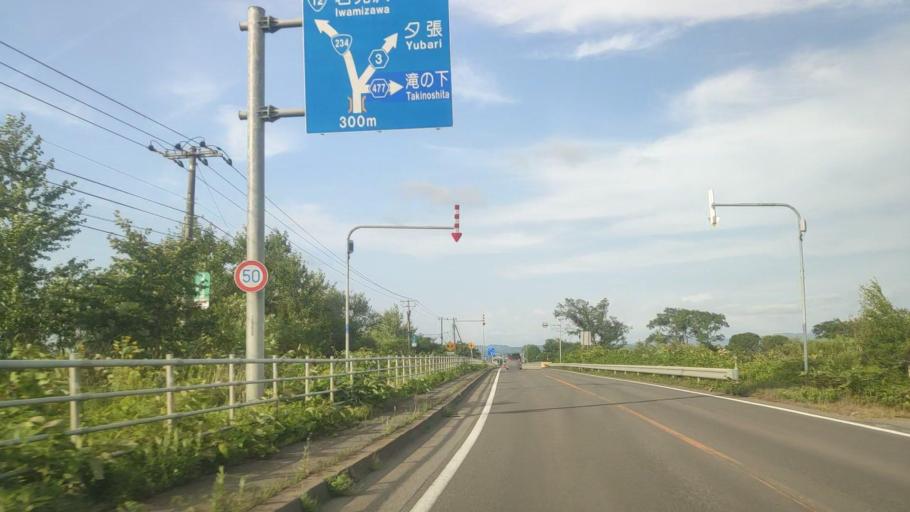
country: JP
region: Hokkaido
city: Iwamizawa
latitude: 43.0234
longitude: 141.8071
